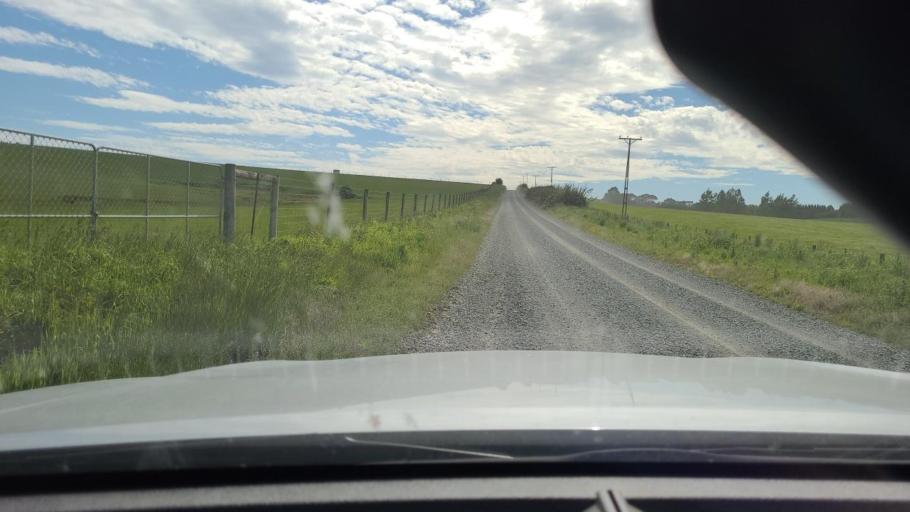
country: NZ
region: Southland
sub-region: Southland District
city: Riverton
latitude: -46.0006
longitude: 167.7816
